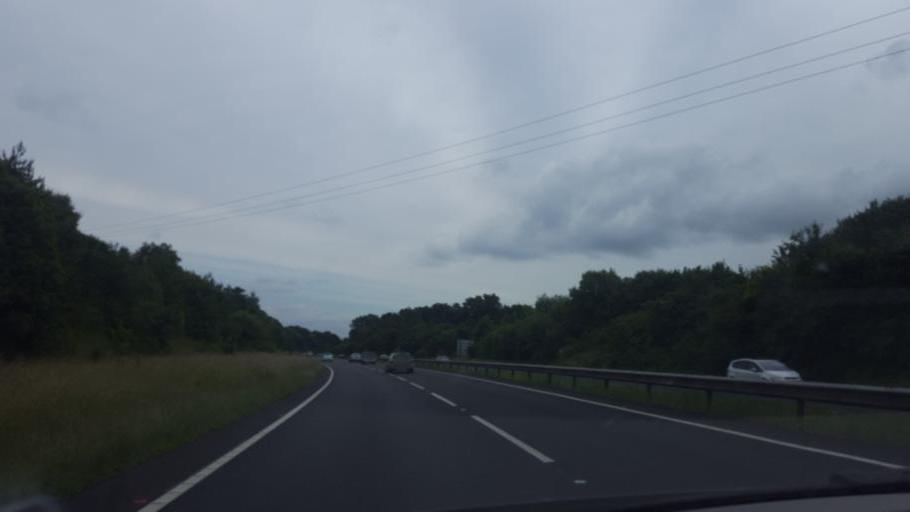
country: GB
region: England
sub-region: Royal Borough of Windsor and Maidenhead
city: Bisham
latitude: 51.5254
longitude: -0.7787
